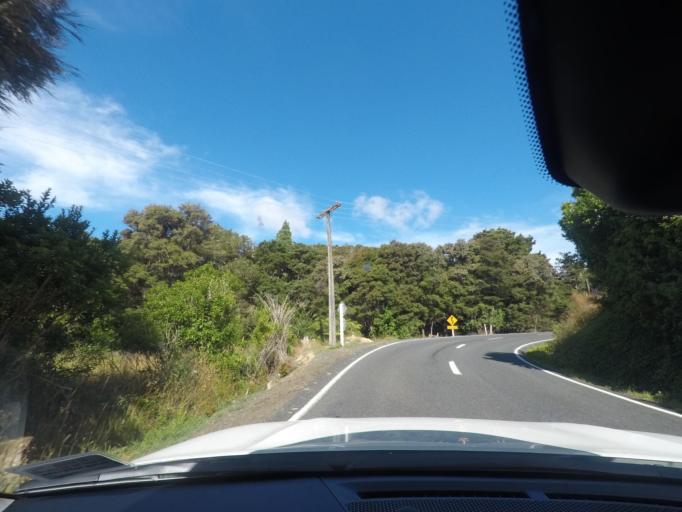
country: NZ
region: Northland
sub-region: Whangarei
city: Ngunguru
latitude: -35.6701
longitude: 174.4576
